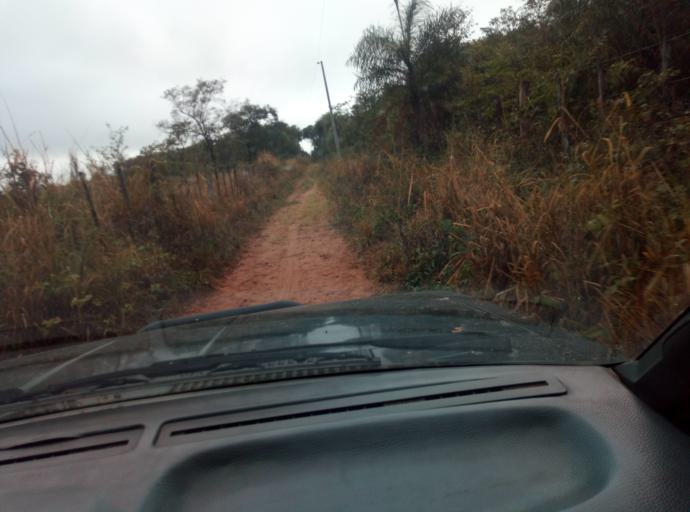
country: PY
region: Caaguazu
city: Carayao
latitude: -25.1916
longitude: -56.3544
